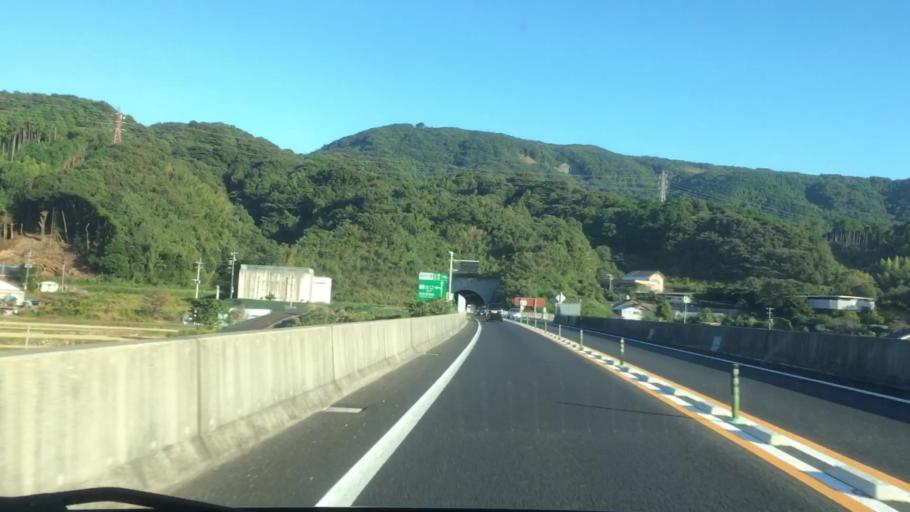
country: JP
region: Nagasaki
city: Sasebo
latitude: 33.1902
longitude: 129.6857
